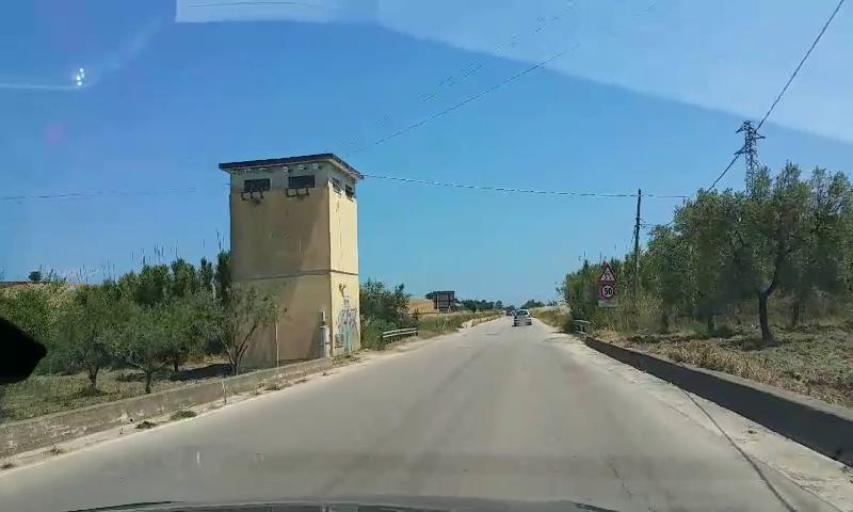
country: IT
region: Molise
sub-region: Provincia di Campobasso
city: San Giacomo degli Schiavoni
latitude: 41.9978
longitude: 14.9536
